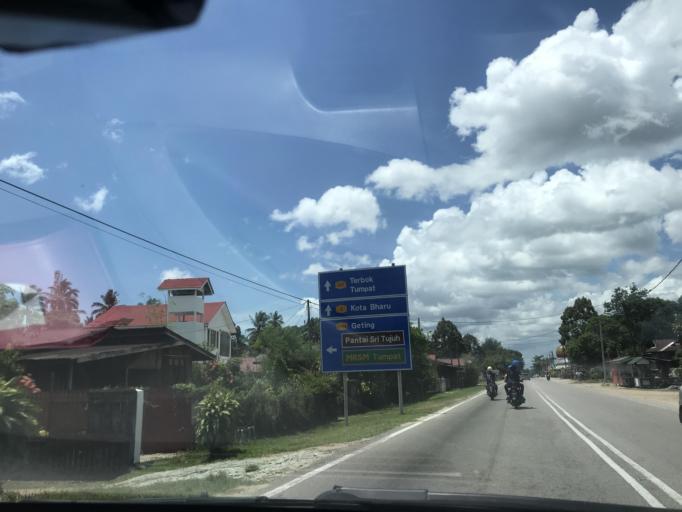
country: MY
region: Kelantan
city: Tumpat
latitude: 6.1928
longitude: 102.1505
